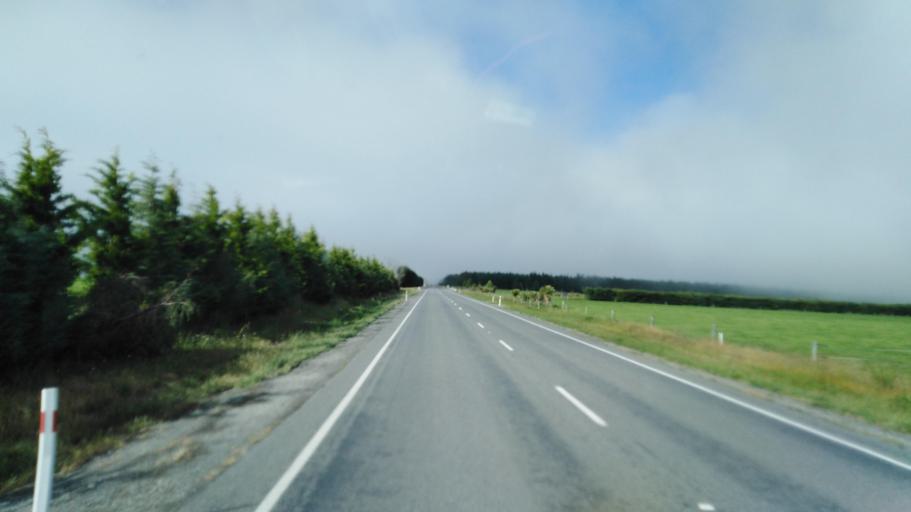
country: NZ
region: Canterbury
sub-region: Hurunui District
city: Amberley
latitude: -42.8118
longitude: 172.8180
